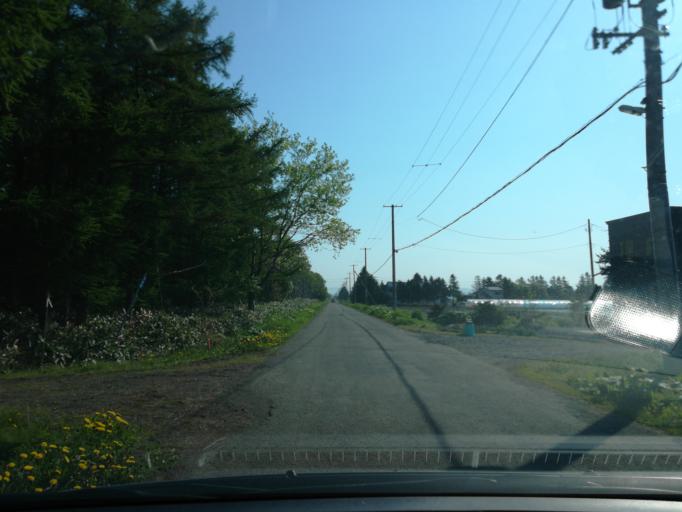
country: JP
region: Hokkaido
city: Ebetsu
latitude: 43.1207
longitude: 141.6562
